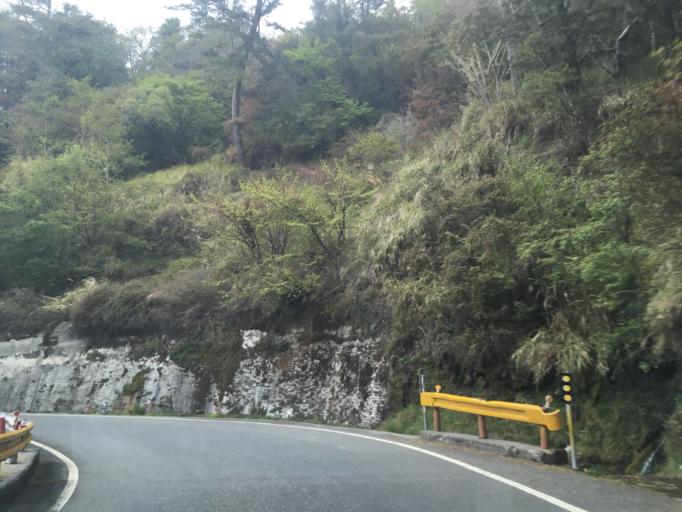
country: TW
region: Taiwan
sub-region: Hualien
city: Hualian
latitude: 24.1874
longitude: 121.3282
